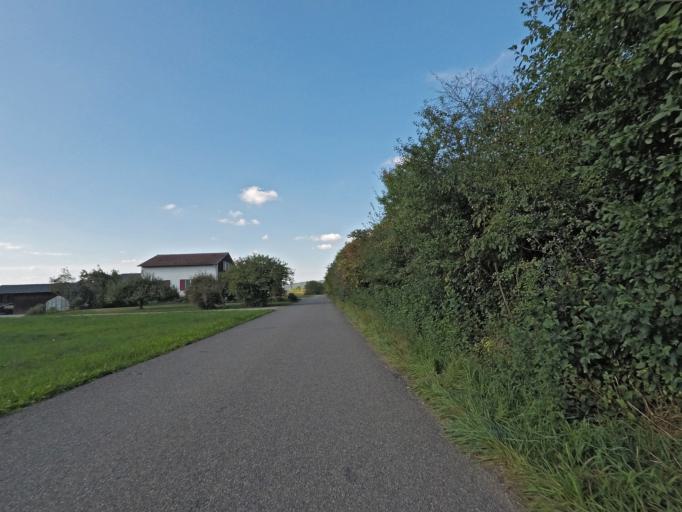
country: CH
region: Thurgau
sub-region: Frauenfeld District
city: Diessenhofen
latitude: 47.6580
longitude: 8.7473
